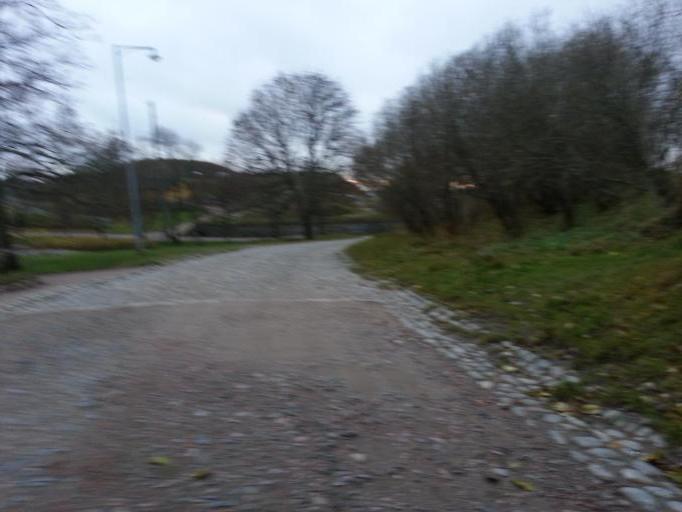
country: FI
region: Uusimaa
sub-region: Helsinki
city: Helsinki
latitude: 60.1418
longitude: 24.9860
